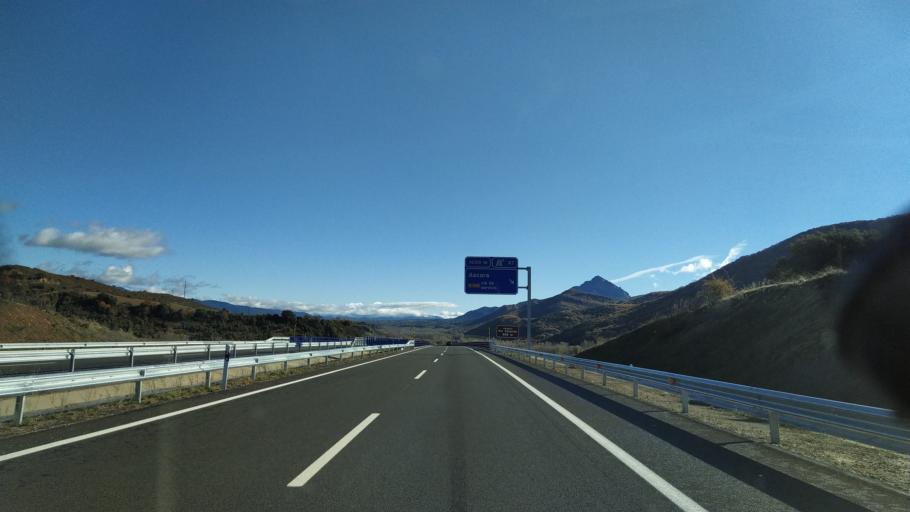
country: ES
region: Aragon
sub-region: Provincia de Huesca
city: Santa Cruz de la Seros
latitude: 42.5624
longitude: -0.6736
